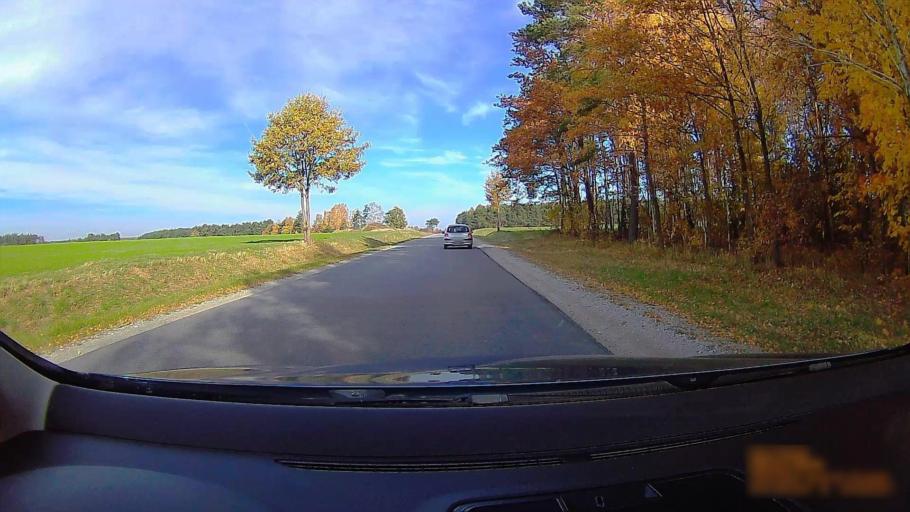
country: PL
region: Greater Poland Voivodeship
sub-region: Powiat ostrzeszowski
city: Doruchow
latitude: 51.3711
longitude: 18.0349
